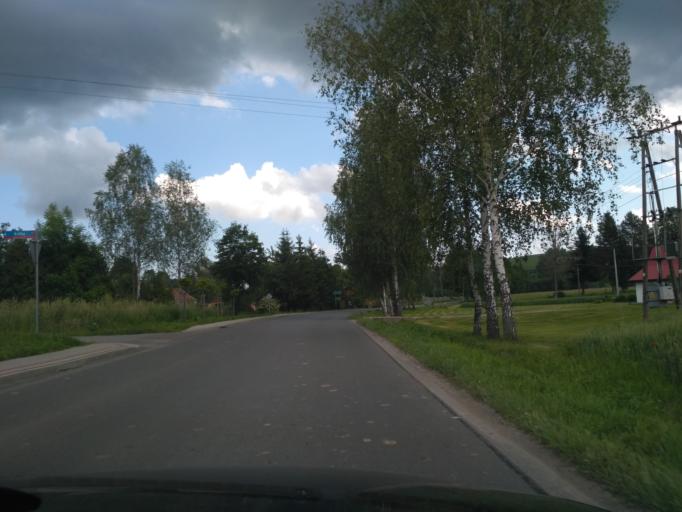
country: PL
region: Subcarpathian Voivodeship
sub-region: Powiat rzeszowski
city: Blazowa
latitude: 49.9387
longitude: 22.0911
